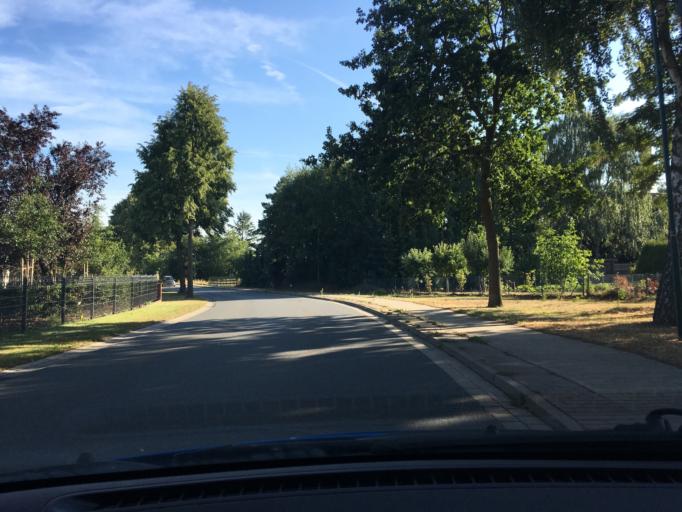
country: DE
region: Lower Saxony
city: Thomasburg
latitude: 53.1949
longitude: 10.6349
